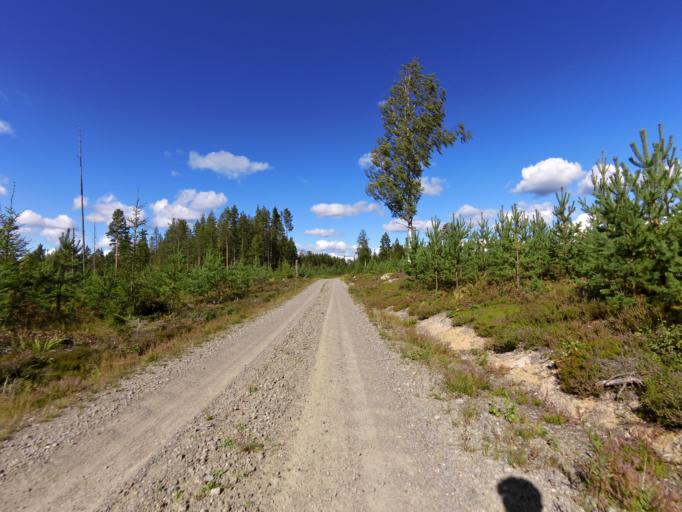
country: SE
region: Gaevleborg
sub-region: Ockelbo Kommun
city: Ockelbo
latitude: 60.8172
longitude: 16.7578
